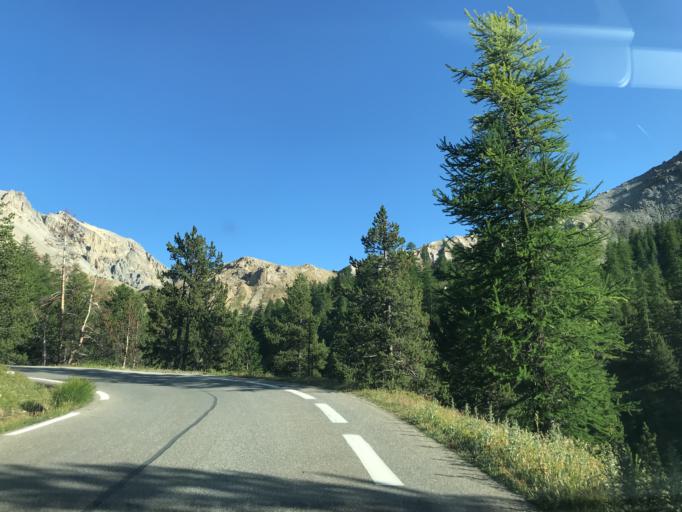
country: FR
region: Provence-Alpes-Cote d'Azur
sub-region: Departement des Hautes-Alpes
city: Villar-Saint-Pancrace
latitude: 44.8265
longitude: 6.7279
